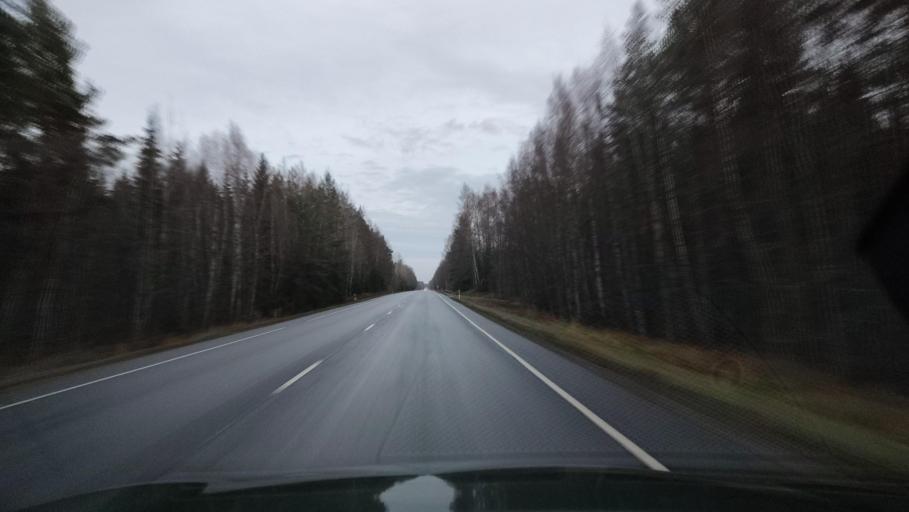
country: FI
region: Ostrobothnia
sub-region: Vaasa
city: Ristinummi
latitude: 63.0034
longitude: 21.7637
